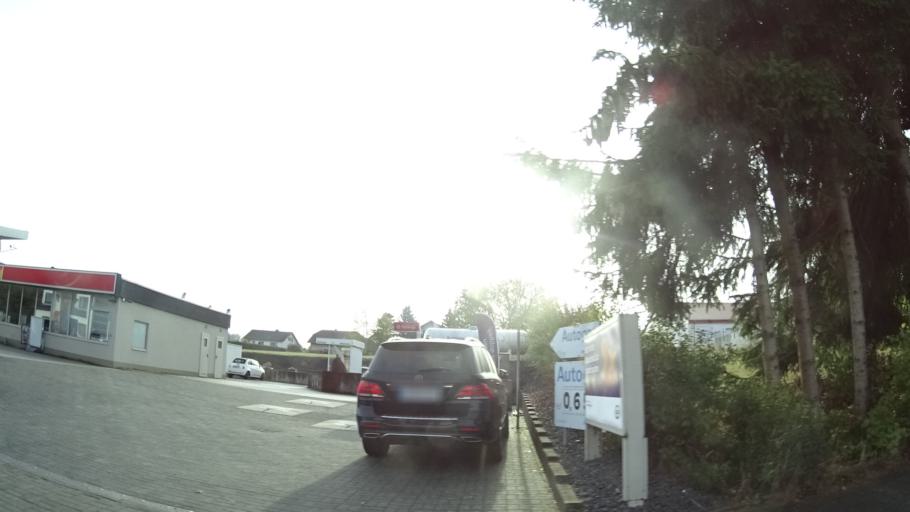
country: DE
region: Hesse
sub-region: Regierungsbezirk Kassel
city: Hosenfeld
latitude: 50.5004
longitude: 9.4759
